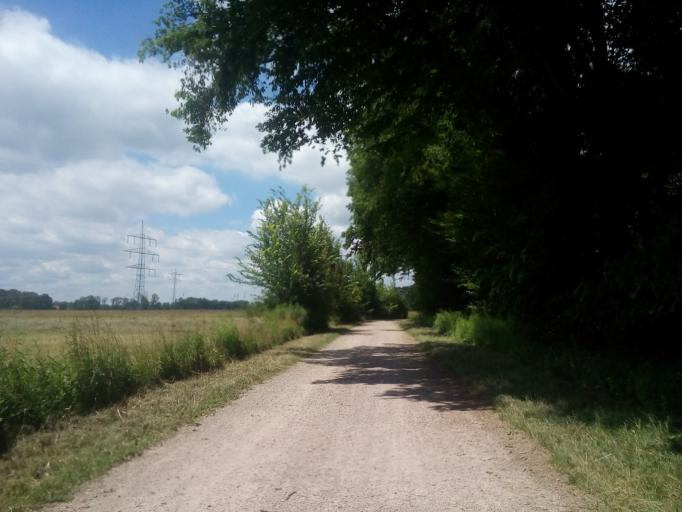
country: DE
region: Baden-Wuerttemberg
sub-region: Freiburg Region
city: Rheinau
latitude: 48.6434
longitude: 7.9457
